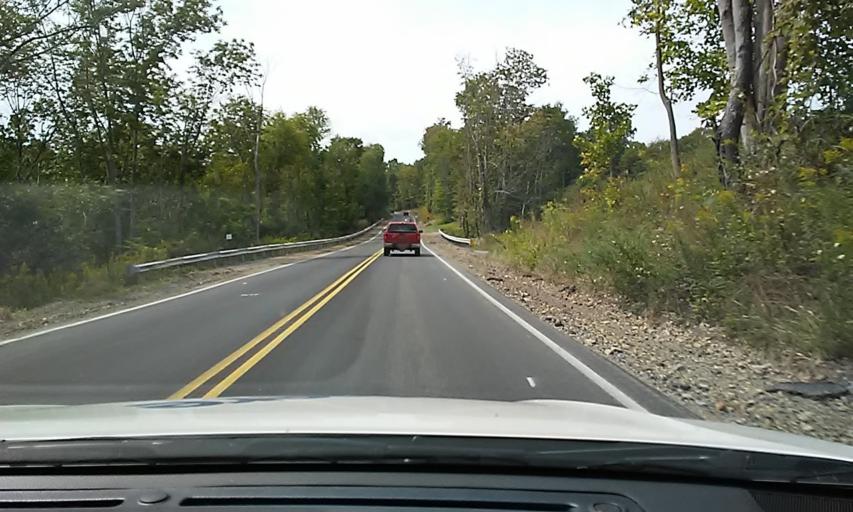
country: US
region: Pennsylvania
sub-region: Clearfield County
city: Treasure Lake
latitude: 41.1837
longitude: -78.6345
